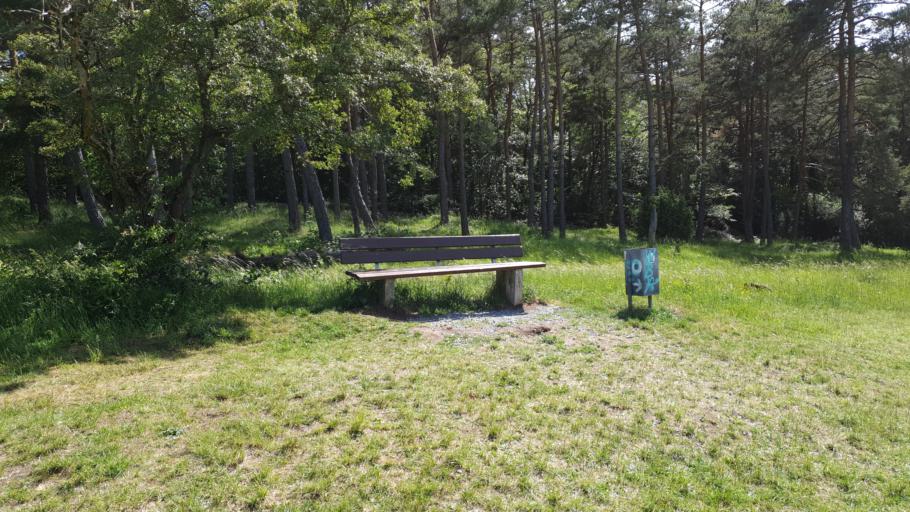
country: DE
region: Baden-Wuerttemberg
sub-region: Regierungsbezirk Stuttgart
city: Leonberg
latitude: 48.7965
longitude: 9.0352
